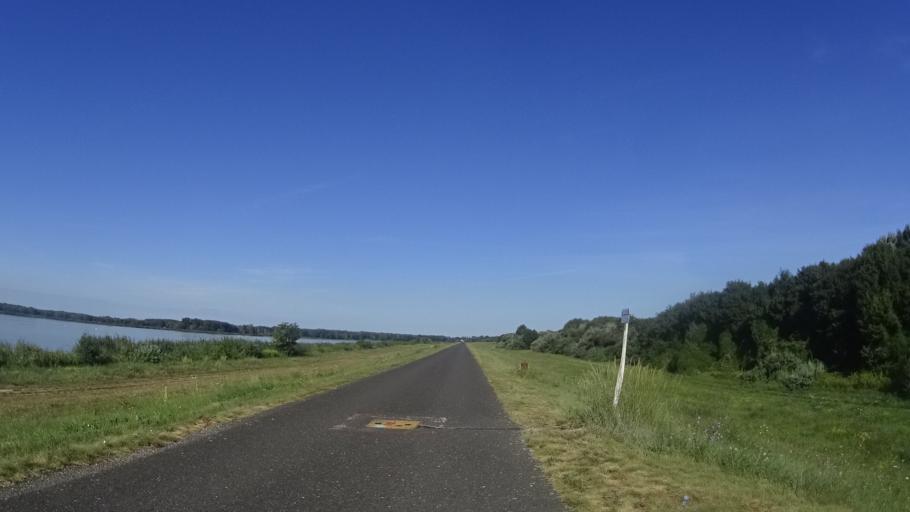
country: SK
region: Bratislavsky
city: Dunajska Luzna
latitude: 48.0598
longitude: 17.2079
